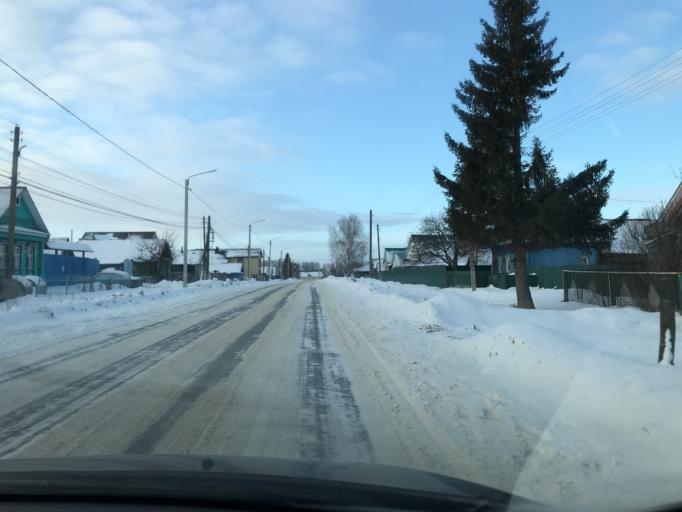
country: RU
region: Ulyanovsk
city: Undory
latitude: 54.6069
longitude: 48.3978
